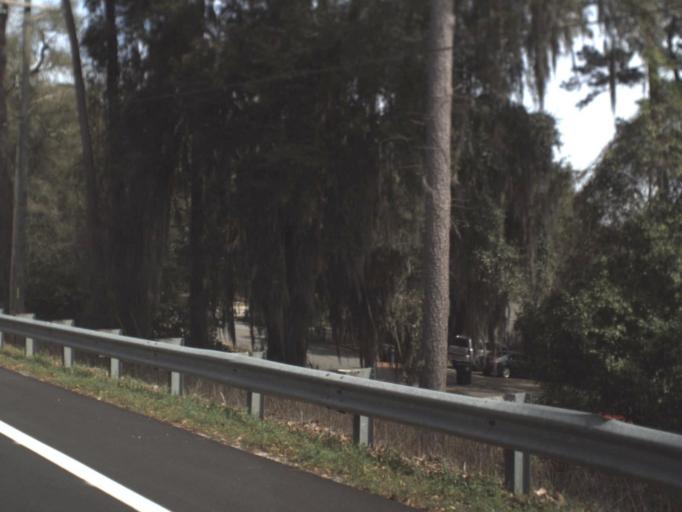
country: US
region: Florida
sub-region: Gadsden County
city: Midway
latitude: 30.5268
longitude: -84.3627
